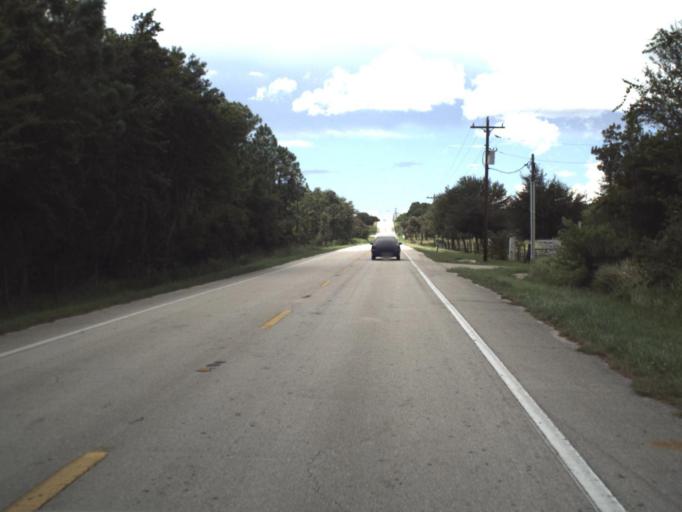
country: US
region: Florida
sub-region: Polk County
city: Fort Meade
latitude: 27.7335
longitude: -81.6844
